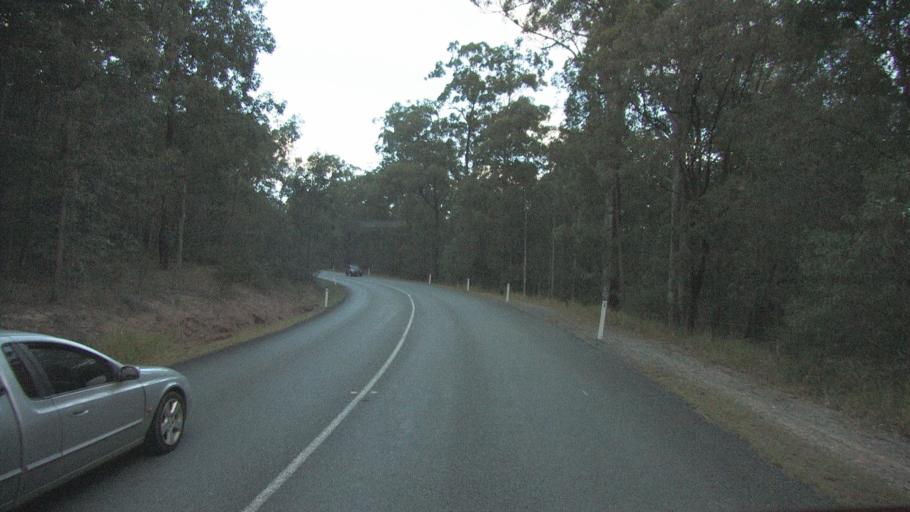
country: AU
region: Queensland
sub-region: Logan
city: Chambers Flat
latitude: -27.7991
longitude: 153.1426
